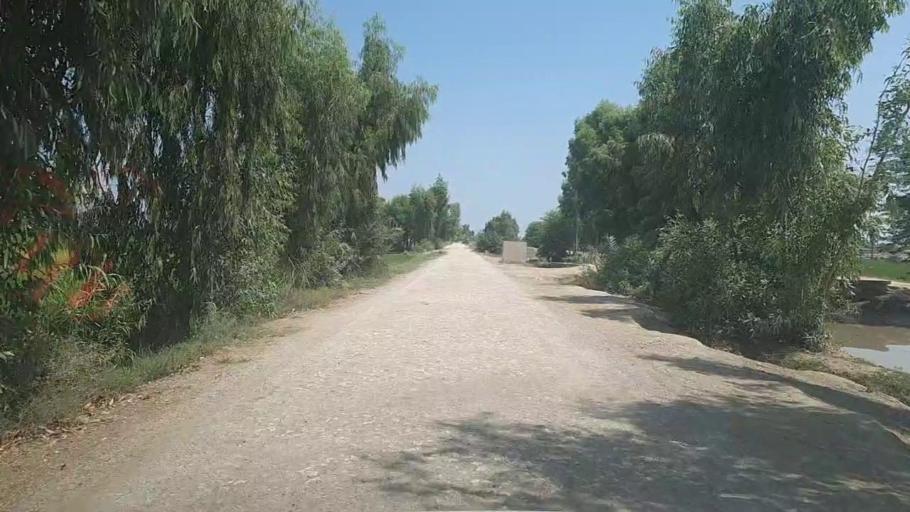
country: PK
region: Sindh
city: Kandhkot
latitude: 28.2705
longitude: 69.2209
